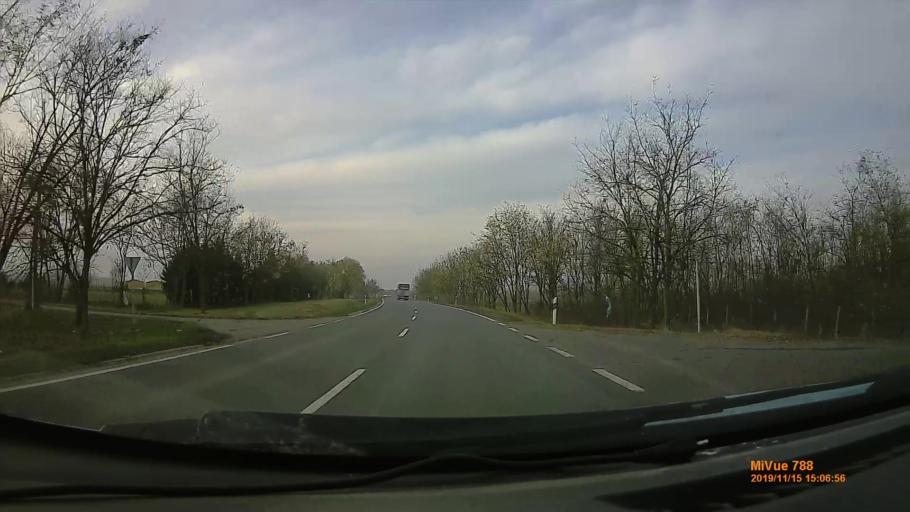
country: HU
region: Bekes
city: Gyula
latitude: 46.6478
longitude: 21.2406
